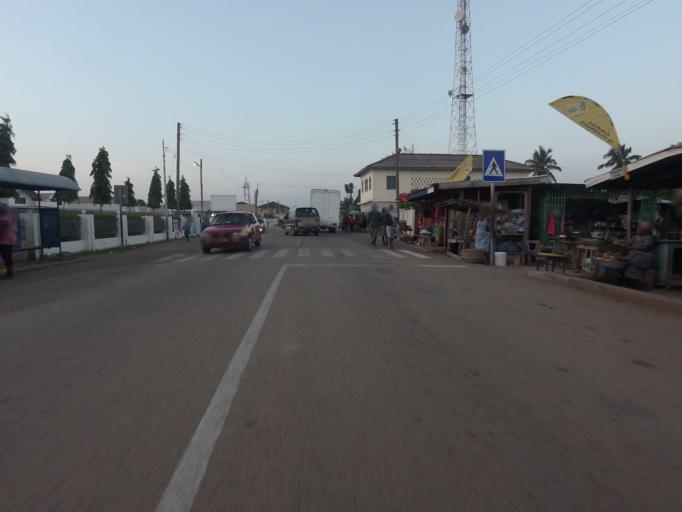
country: GH
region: Volta
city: Keta
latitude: 5.8876
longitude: 0.9832
